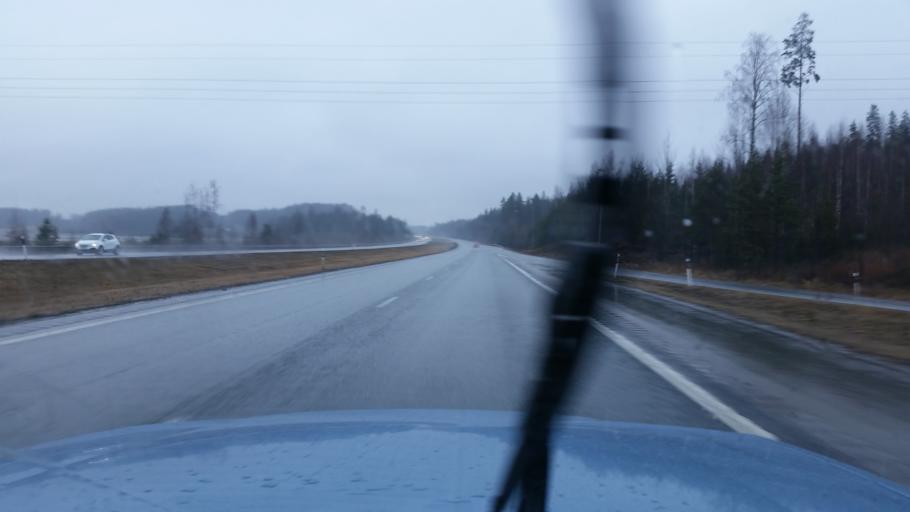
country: FI
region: Haeme
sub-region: Haemeenlinna
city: Tervakoski
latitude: 60.8257
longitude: 24.6645
